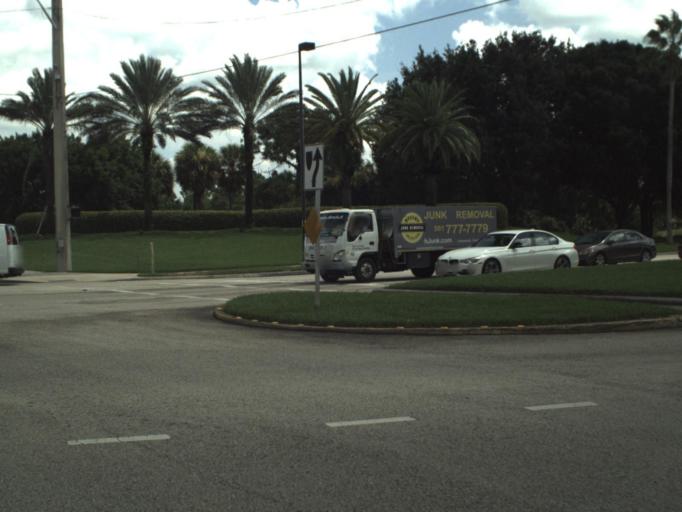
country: US
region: Florida
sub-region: Palm Beach County
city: North Palm Beach
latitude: 26.8510
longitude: -80.0962
